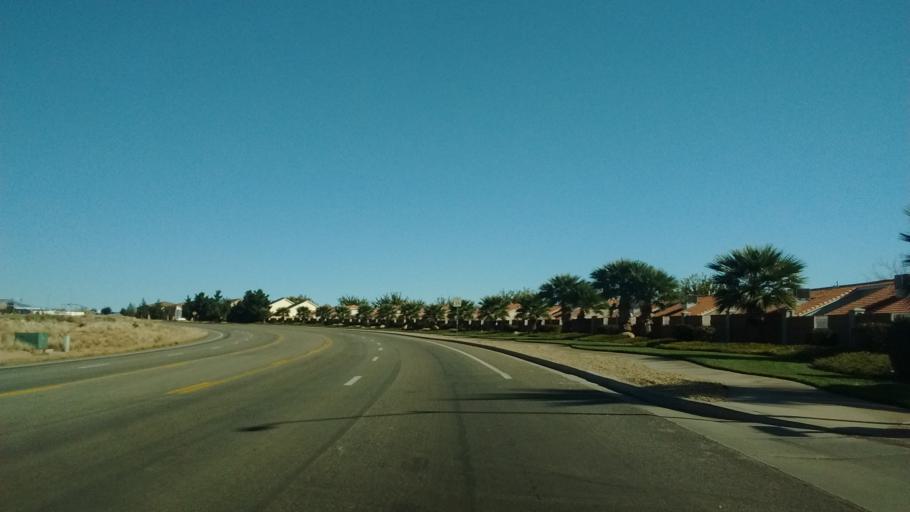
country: US
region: Utah
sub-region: Washington County
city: Washington
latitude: 37.1571
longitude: -113.4370
